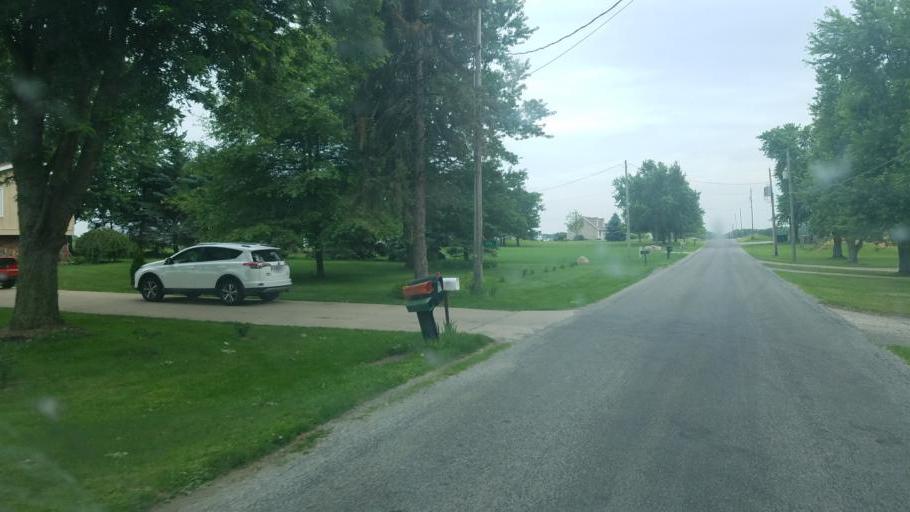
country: US
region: Ohio
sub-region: Wayne County
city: Orrville
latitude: 40.7851
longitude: -81.7753
